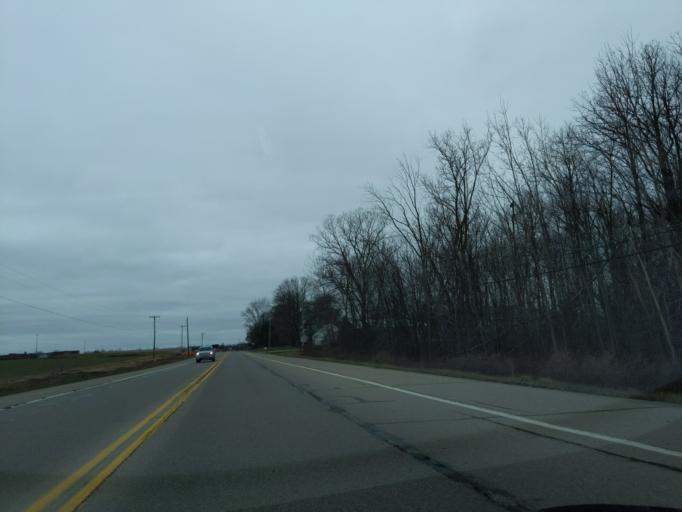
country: US
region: Michigan
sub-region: Clinton County
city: Saint Johns
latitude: 43.0014
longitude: -84.5256
